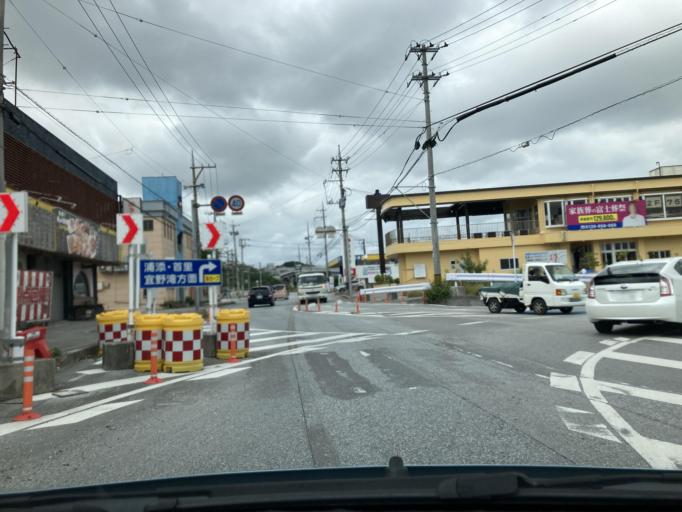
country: JP
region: Okinawa
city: Ginowan
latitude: 26.2394
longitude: 127.7451
